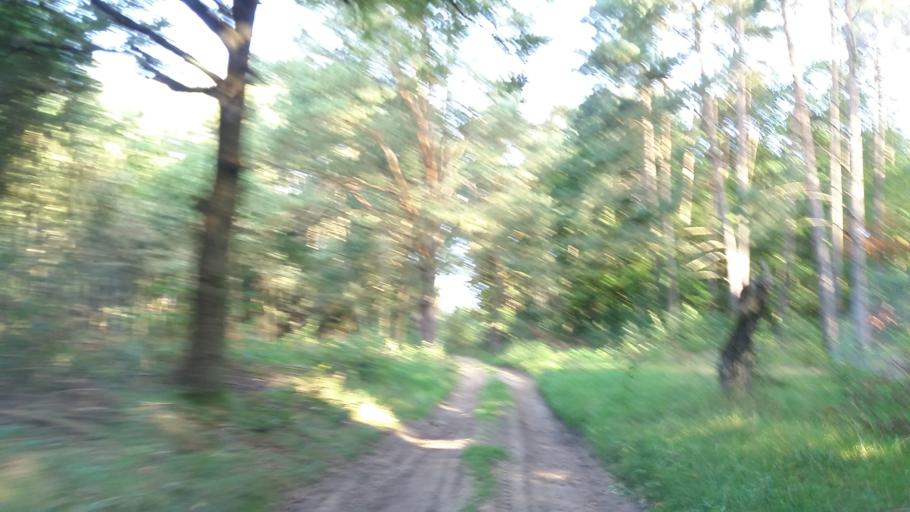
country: PL
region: West Pomeranian Voivodeship
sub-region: Powiat choszczenski
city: Recz
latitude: 53.1989
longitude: 15.5424
